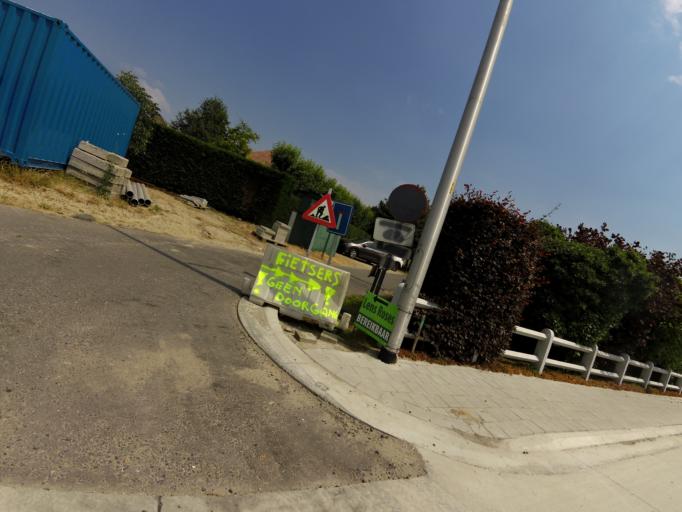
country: BE
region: Flanders
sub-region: Provincie West-Vlaanderen
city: Oudenburg
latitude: 51.1787
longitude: 3.0052
